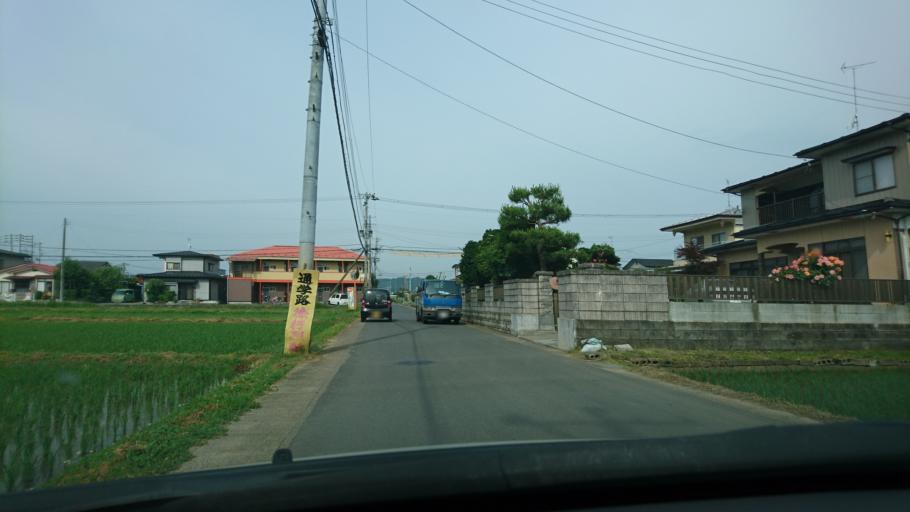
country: JP
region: Iwate
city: Ichinoseki
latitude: 38.9200
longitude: 141.1116
